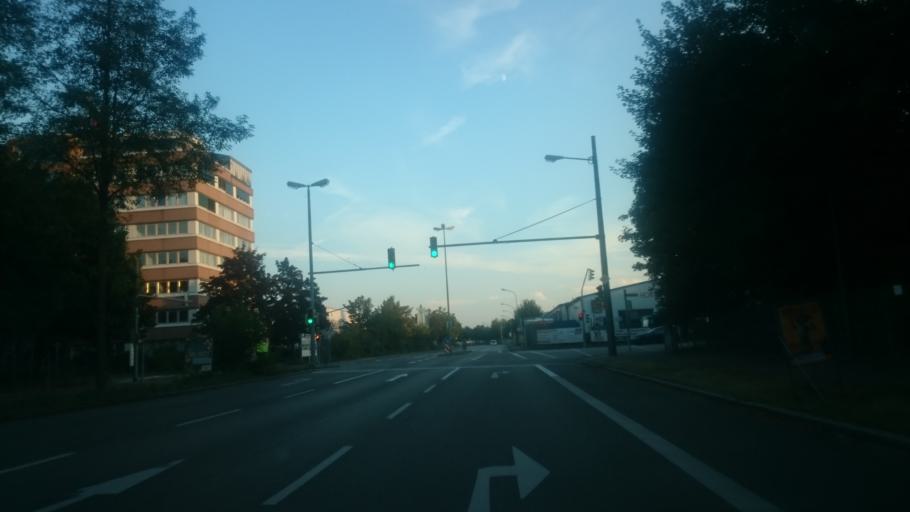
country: DE
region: Bavaria
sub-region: Swabia
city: Augsburg
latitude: 48.3961
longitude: 10.9307
